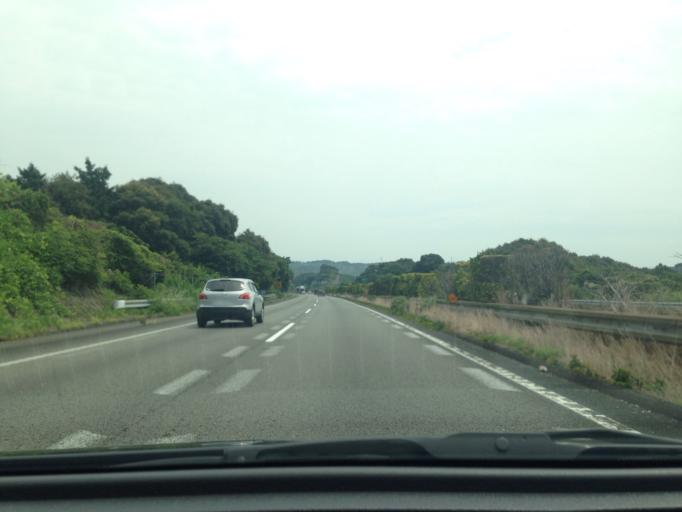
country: JP
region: Shizuoka
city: Shimada
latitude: 34.7551
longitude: 138.1858
